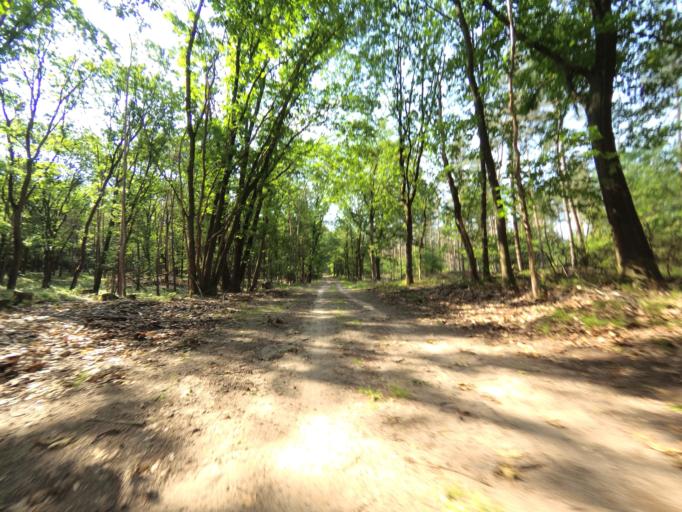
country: NL
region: Gelderland
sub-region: Gemeente Apeldoorn
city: Beekbergen
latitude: 52.1417
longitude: 5.9362
